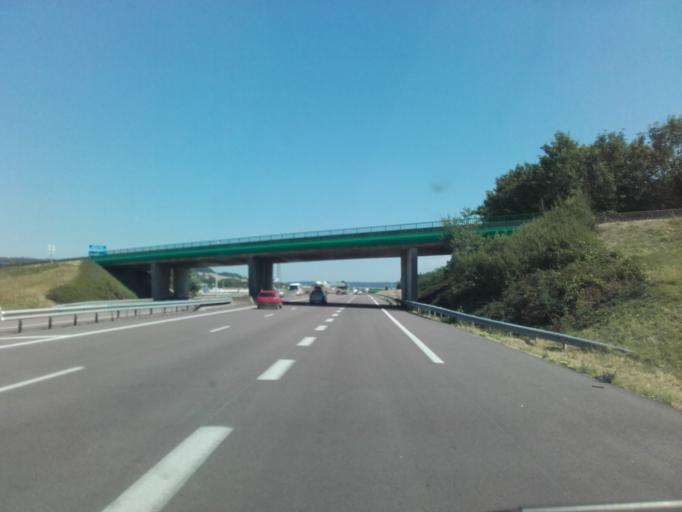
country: FR
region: Bourgogne
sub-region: Departement de la Cote-d'Or
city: Pouilly-en-Auxois
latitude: 47.2520
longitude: 4.5553
